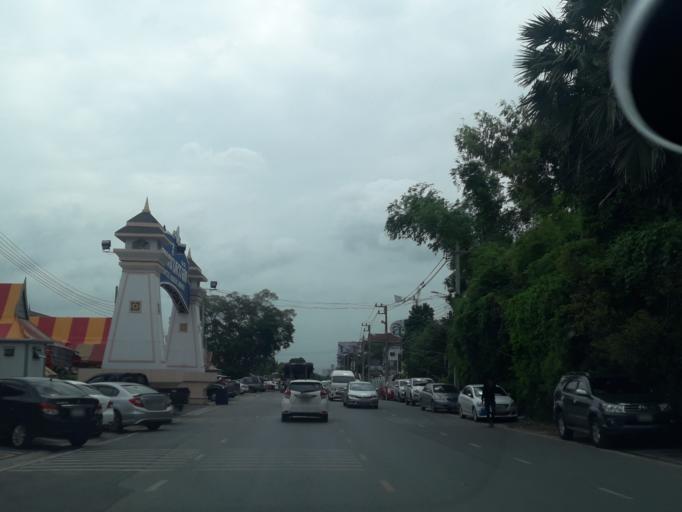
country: TH
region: Bangkok
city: Sai Mai
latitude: 13.9875
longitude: 100.6338
